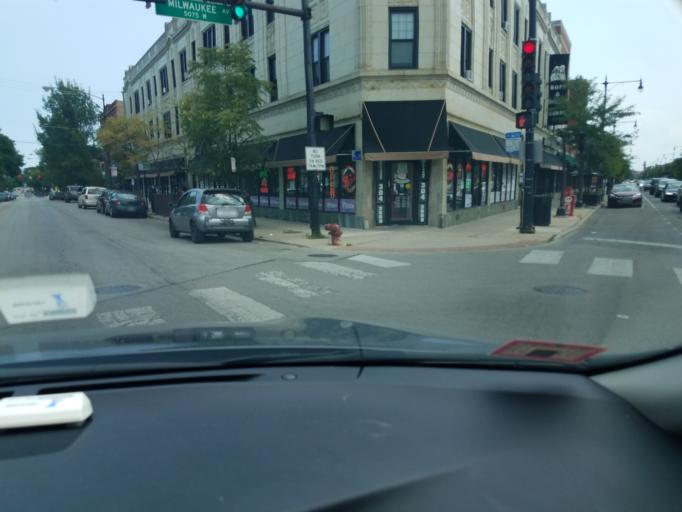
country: US
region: Illinois
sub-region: Cook County
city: Lincolnwood
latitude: 41.9606
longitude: -87.7544
